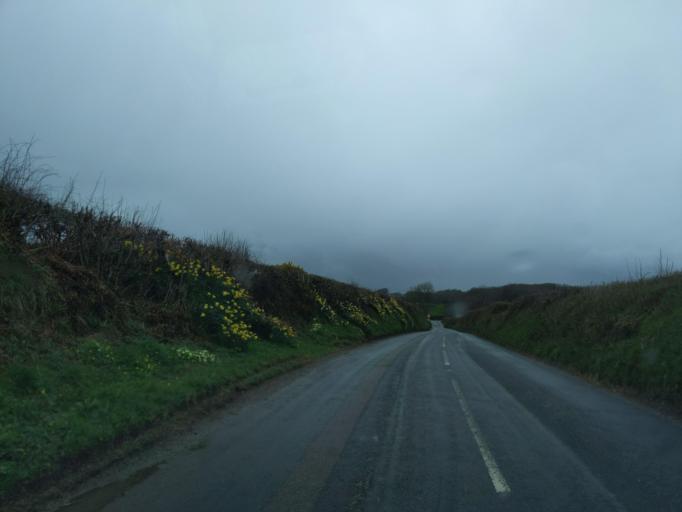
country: GB
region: England
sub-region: Cornwall
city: North Hill
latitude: 50.5856
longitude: -4.4355
